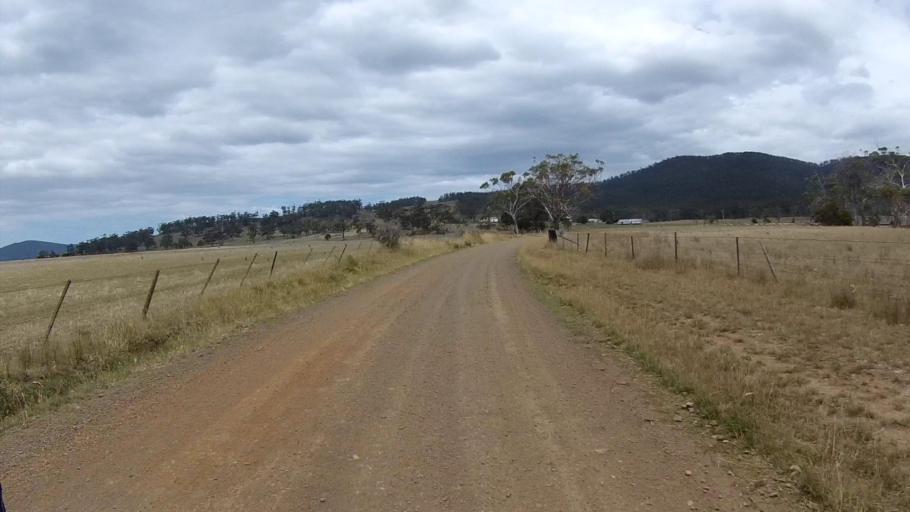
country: AU
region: Tasmania
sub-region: Sorell
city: Sorell
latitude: -42.6561
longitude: 147.9387
